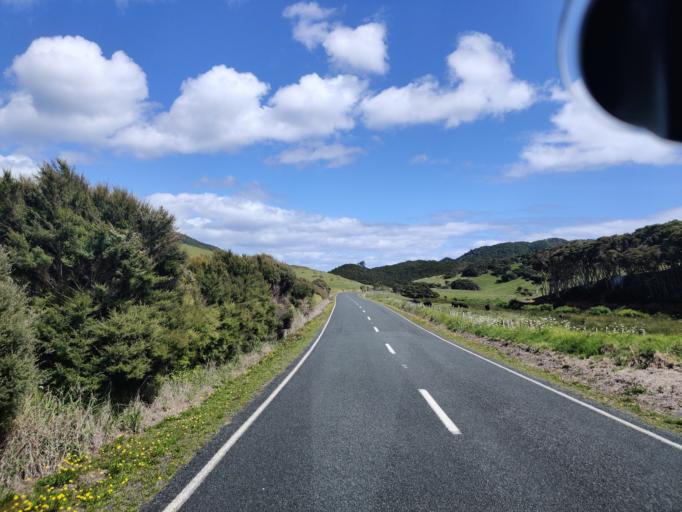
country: NZ
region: Northland
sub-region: Far North District
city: Paihia
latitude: -35.2731
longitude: 174.2813
